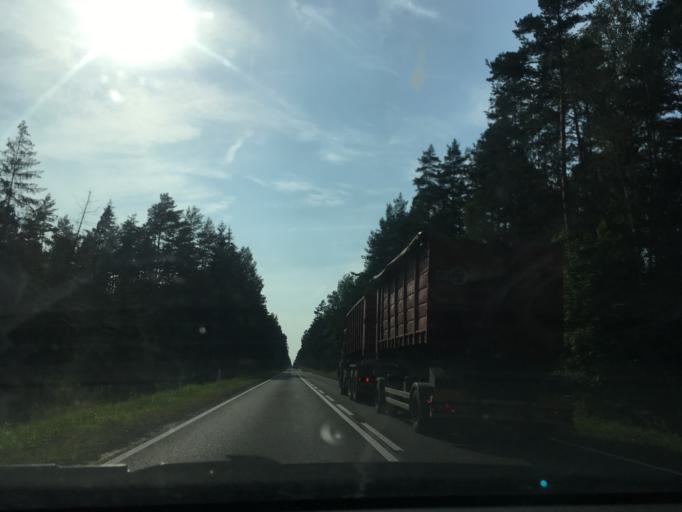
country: PL
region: Podlasie
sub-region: Powiat bialostocki
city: Suprasl
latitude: 53.1257
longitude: 23.4076
